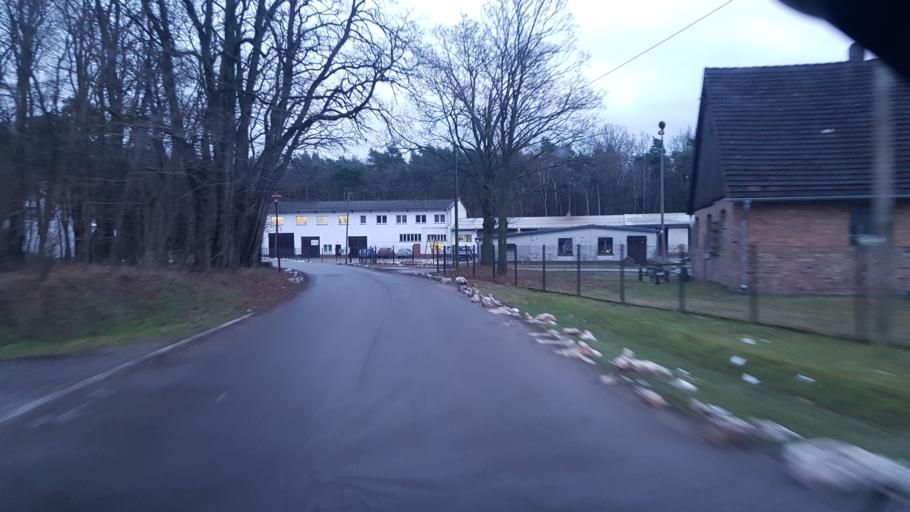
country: DE
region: Brandenburg
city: Tauche
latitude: 52.1119
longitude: 14.1832
